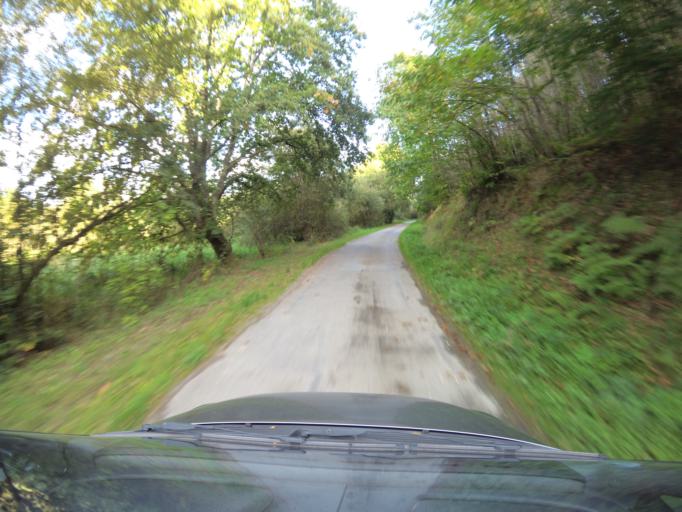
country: FR
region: Brittany
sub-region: Departement du Morbihan
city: Peillac
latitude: 47.7264
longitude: -2.2189
